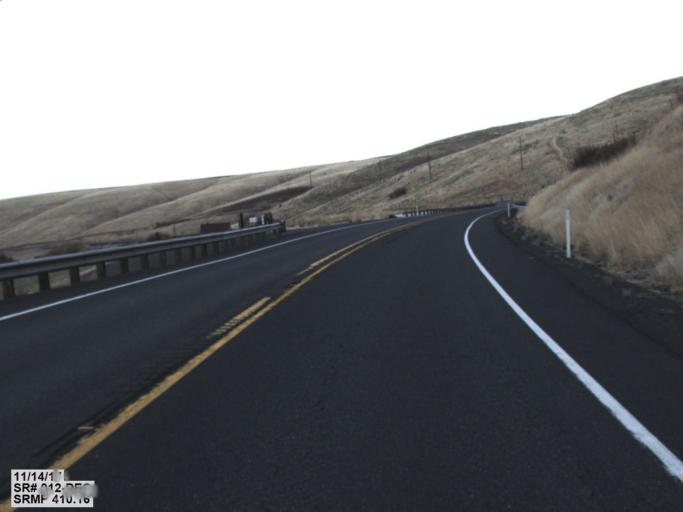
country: US
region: Washington
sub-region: Garfield County
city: Pomeroy
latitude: 46.4565
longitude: -117.4722
